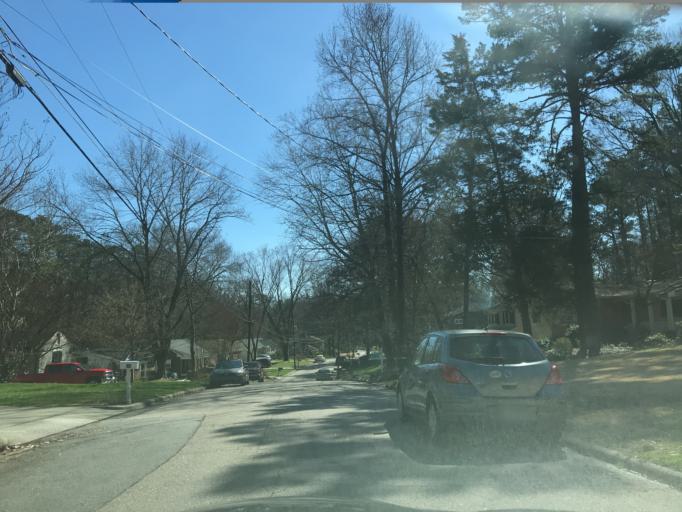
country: US
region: North Carolina
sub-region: Wake County
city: West Raleigh
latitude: 35.8469
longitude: -78.6269
